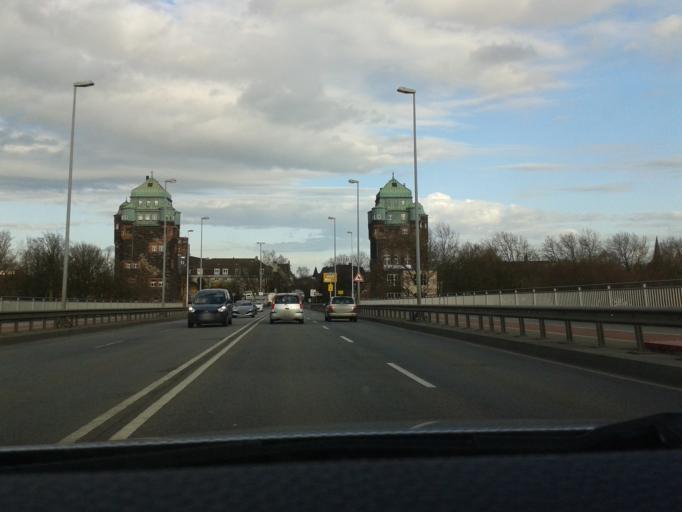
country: DE
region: North Rhine-Westphalia
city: Meiderich
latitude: 51.4560
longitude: 6.7267
